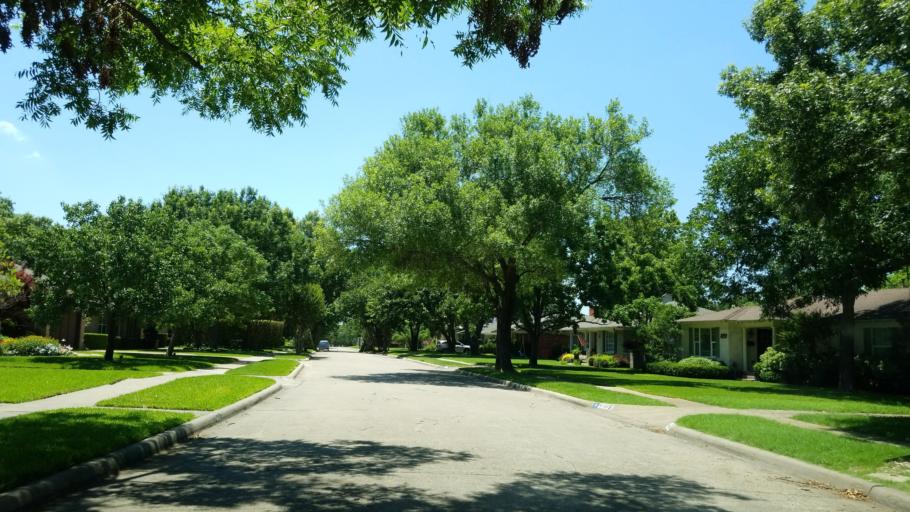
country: US
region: Texas
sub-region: Dallas County
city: University Park
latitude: 32.8770
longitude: -96.8400
